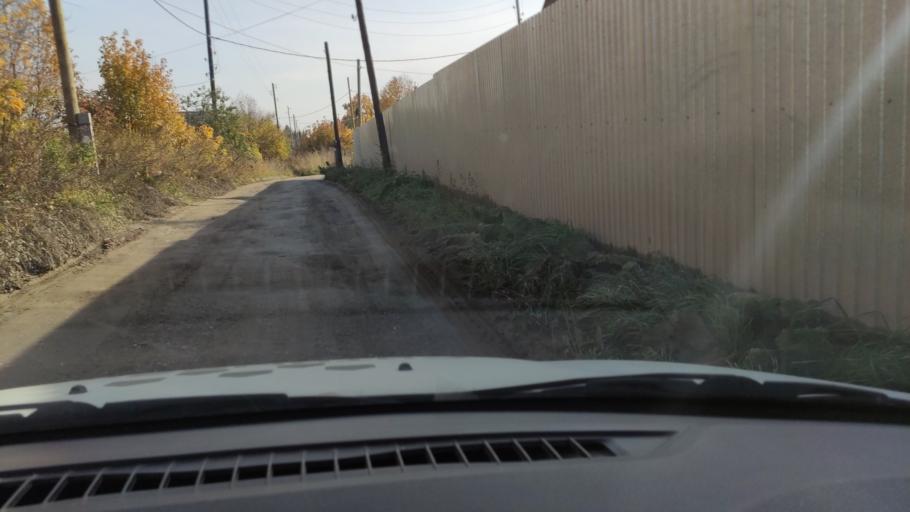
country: RU
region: Perm
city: Sylva
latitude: 58.0471
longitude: 56.7371
